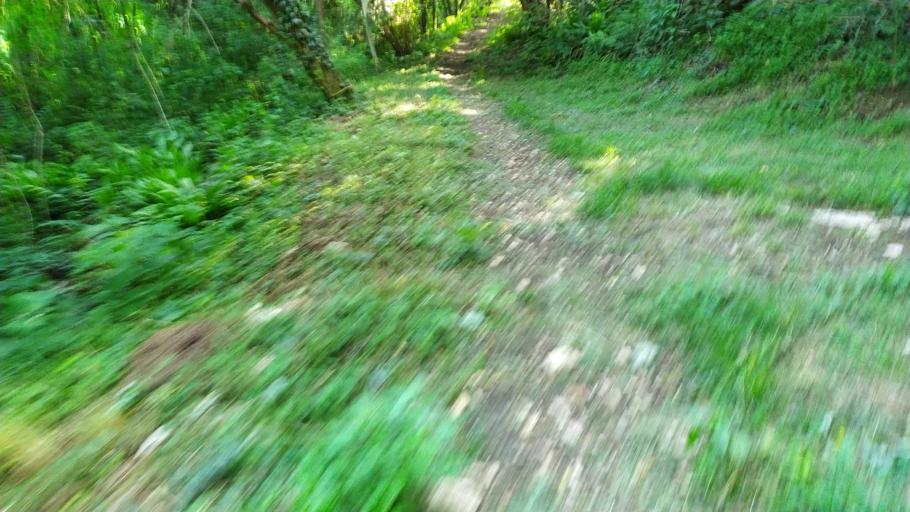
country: IT
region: Veneto
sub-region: Provincia di Vicenza
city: Monte di Malo
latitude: 45.6842
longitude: 11.3508
